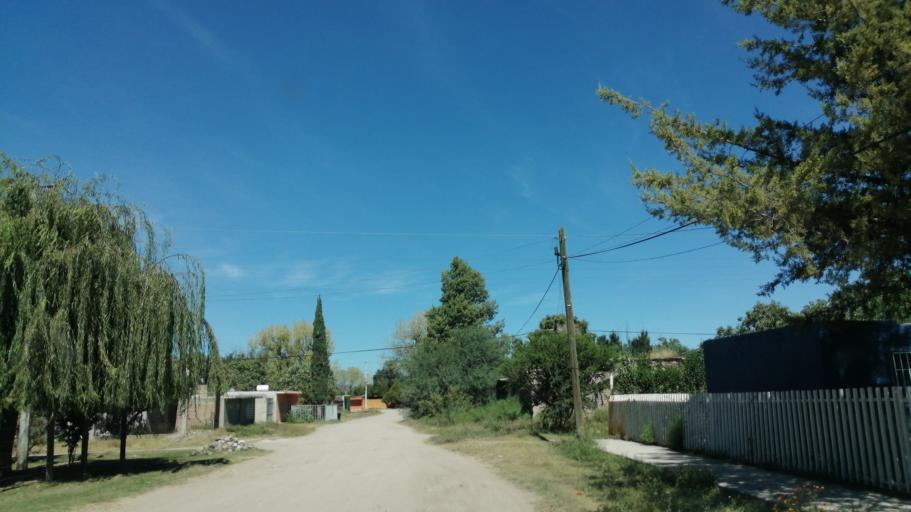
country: MX
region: Durango
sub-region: Santiago Papasquiaro
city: Santiago Papasquiaro
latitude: 25.0333
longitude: -105.4102
